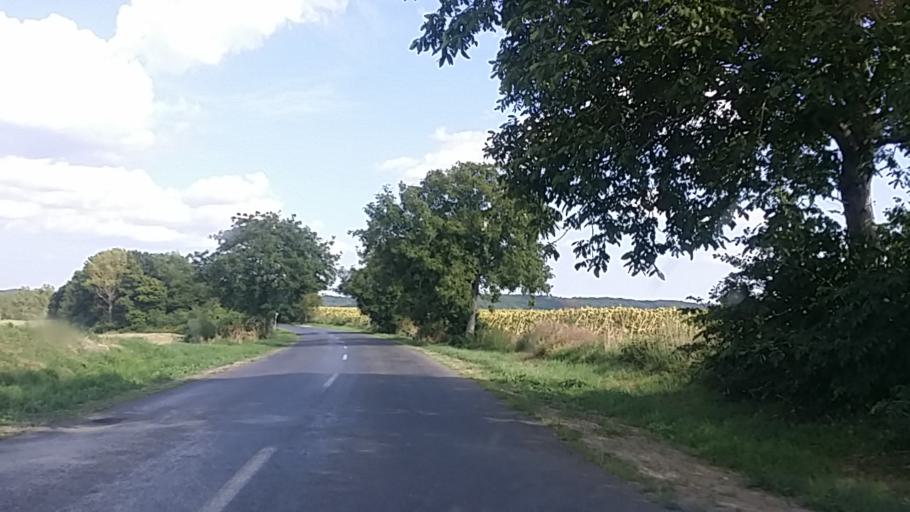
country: HU
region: Tolna
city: Gyonk
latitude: 46.5090
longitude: 18.5492
